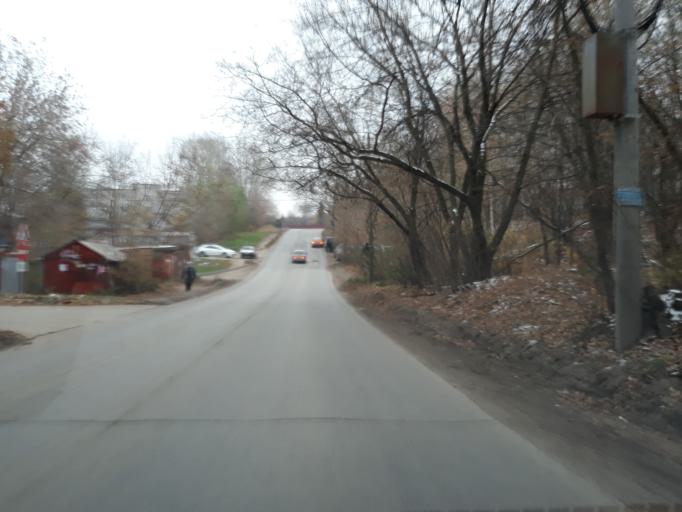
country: RU
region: Nizjnij Novgorod
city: Nizhniy Novgorod
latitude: 56.2447
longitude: 43.9765
